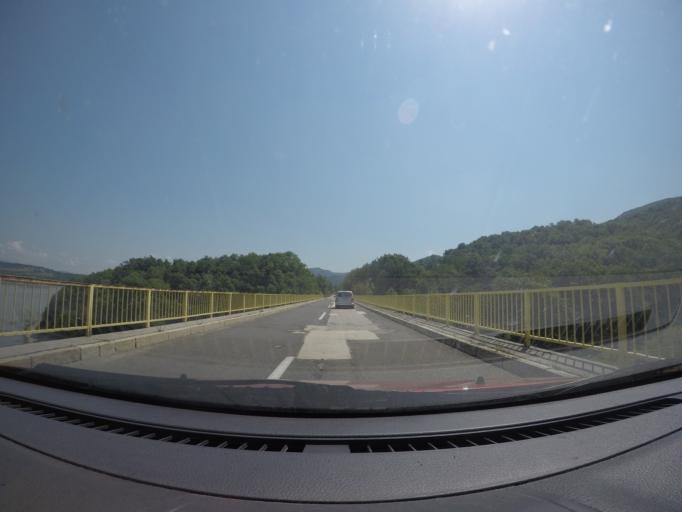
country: RO
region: Mehedinti
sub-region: Comuna Eselnita
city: Eselnita
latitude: 44.6681
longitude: 22.3656
